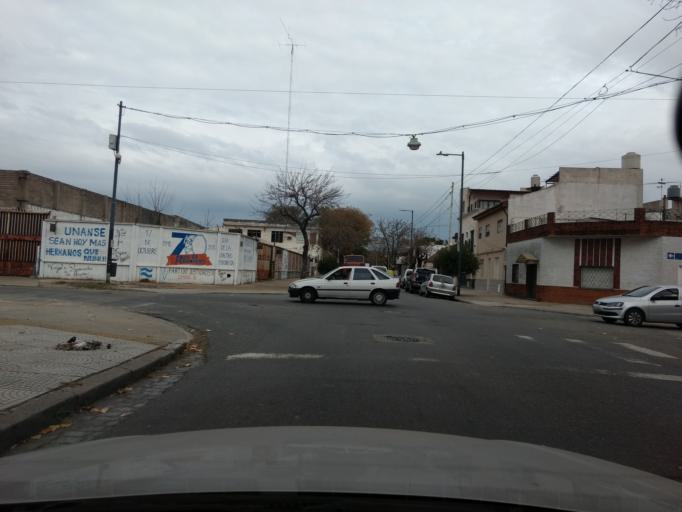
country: AR
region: Buenos Aires F.D.
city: Villa Santa Rita
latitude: -34.6218
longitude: -58.5188
